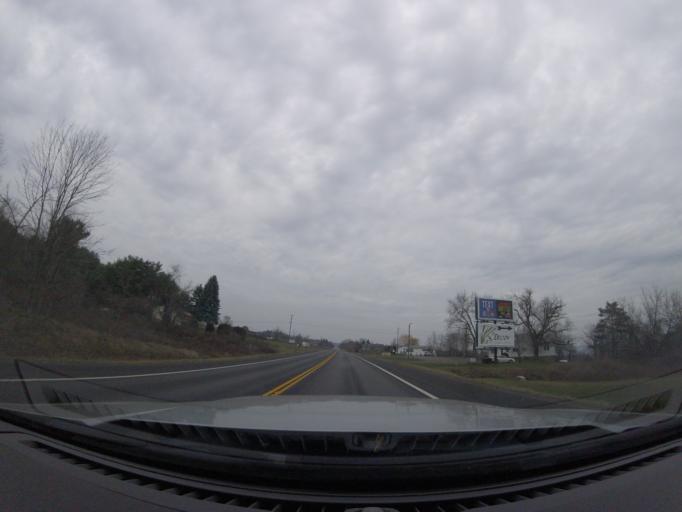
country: US
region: New York
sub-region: Schuyler County
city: Watkins Glen
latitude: 42.4543
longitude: -76.9104
